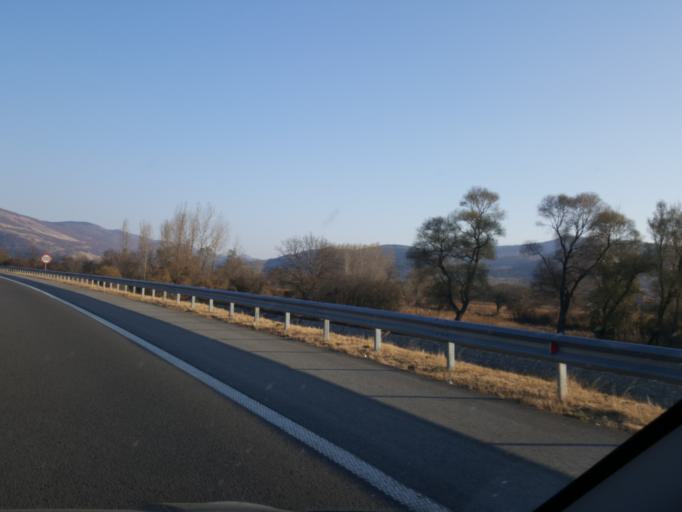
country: RS
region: Central Serbia
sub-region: Pirotski Okrug
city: Dimitrovgrad
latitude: 43.0236
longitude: 22.7280
